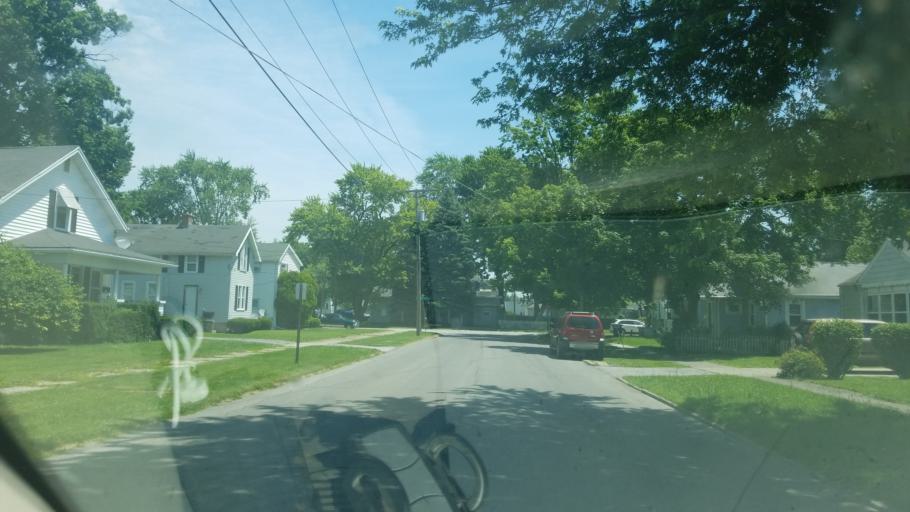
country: US
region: Ohio
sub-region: Hancock County
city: Findlay
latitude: 41.0467
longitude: -83.6423
